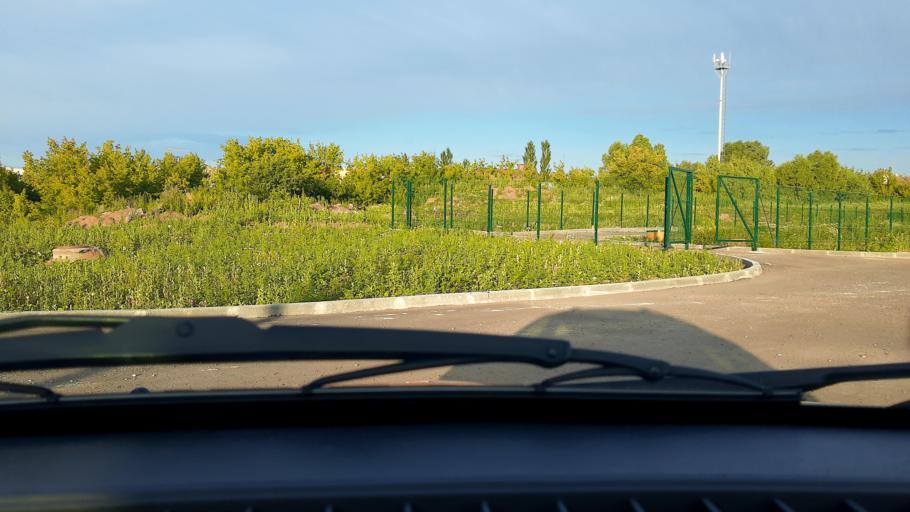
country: RU
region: Bashkortostan
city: Ufa
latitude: 54.8261
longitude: 56.1237
